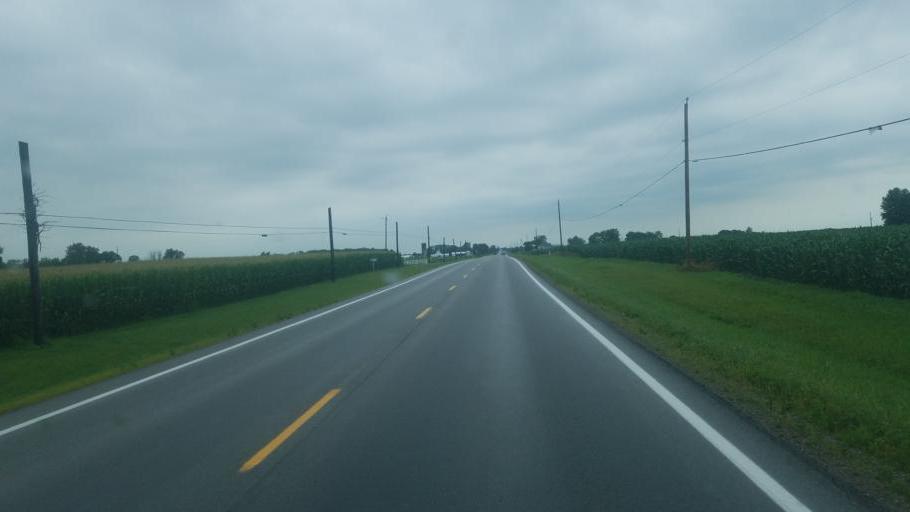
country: US
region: Ohio
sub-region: Hardin County
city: Kenton
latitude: 40.5098
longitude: -83.5017
